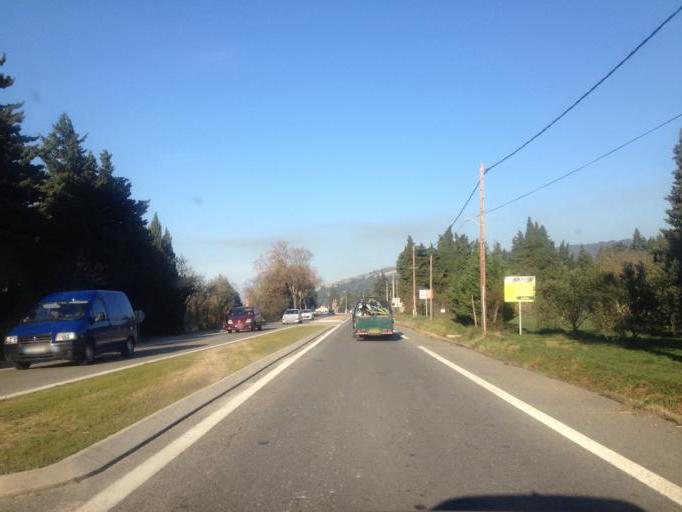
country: FR
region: Provence-Alpes-Cote d'Azur
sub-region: Departement du Vaucluse
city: Mornas
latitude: 44.1938
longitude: 4.7412
